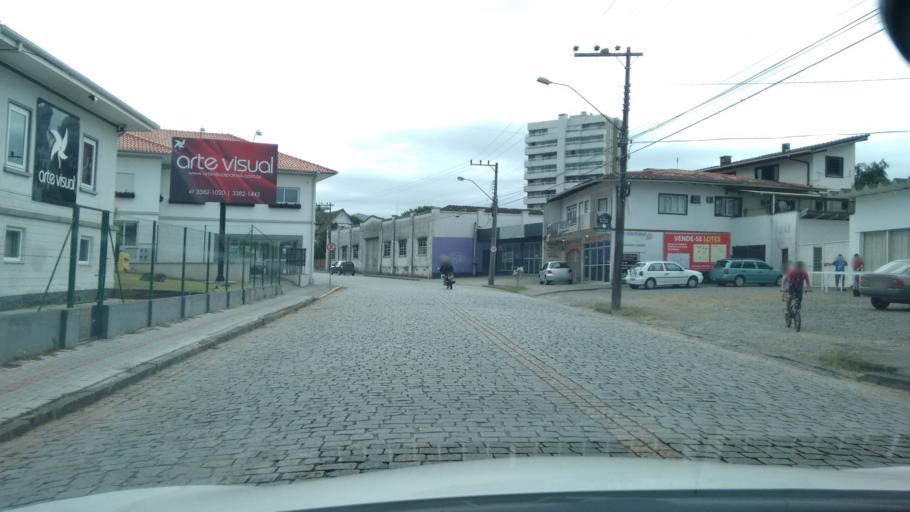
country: BR
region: Santa Catarina
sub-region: Timbo
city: Timbo
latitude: -26.8281
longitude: -49.2684
